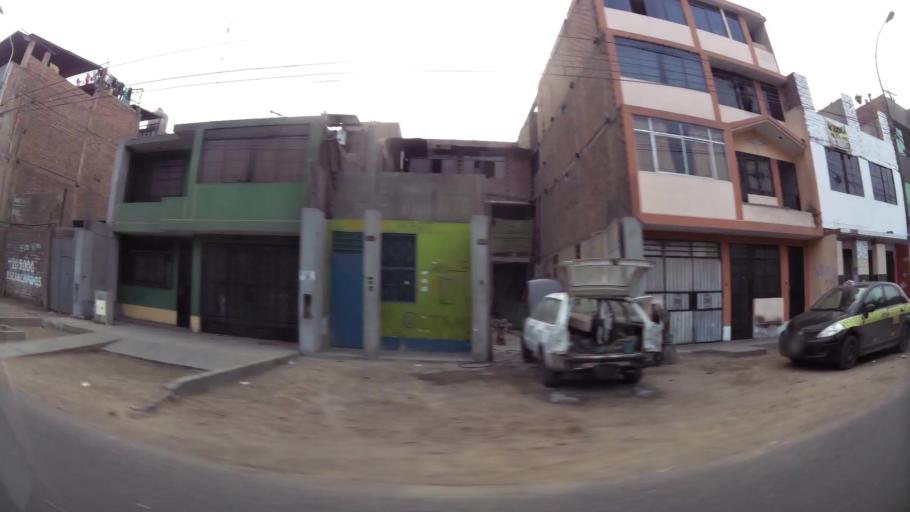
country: PE
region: Lima
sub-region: Lima
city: Independencia
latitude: -11.9892
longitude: -77.0047
